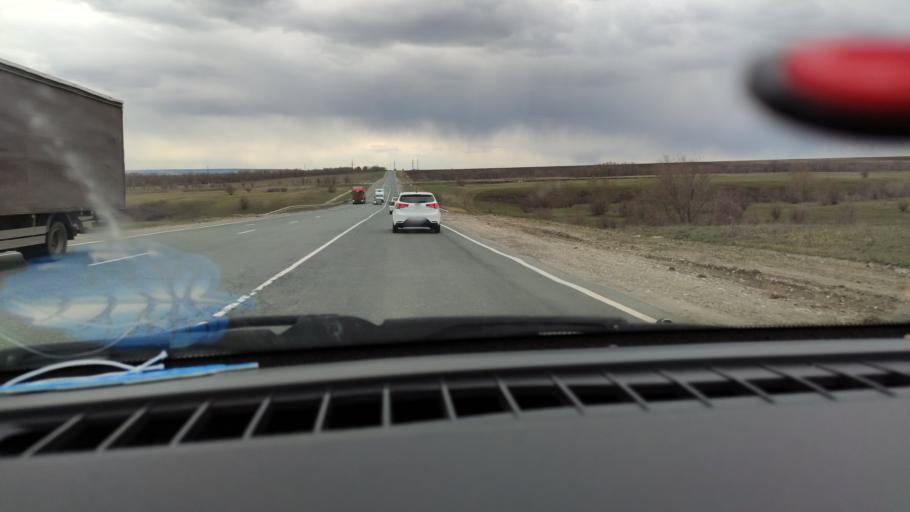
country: RU
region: Saratov
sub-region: Saratovskiy Rayon
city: Saratov
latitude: 51.7537
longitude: 46.0633
